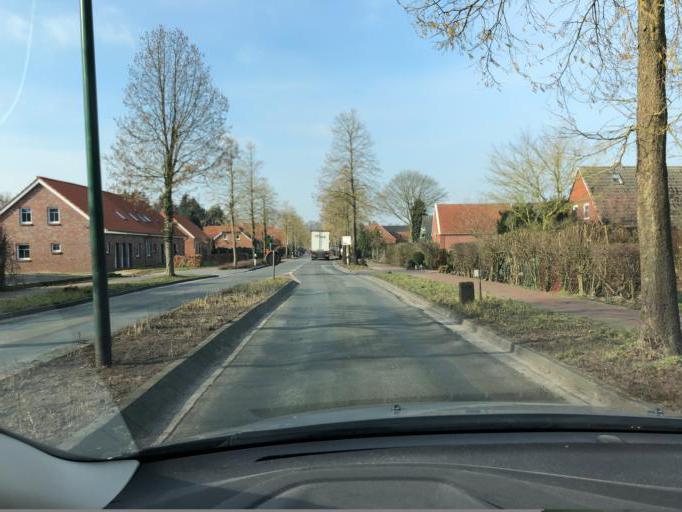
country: DE
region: Lower Saxony
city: Hesel
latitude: 53.3056
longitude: 7.5985
